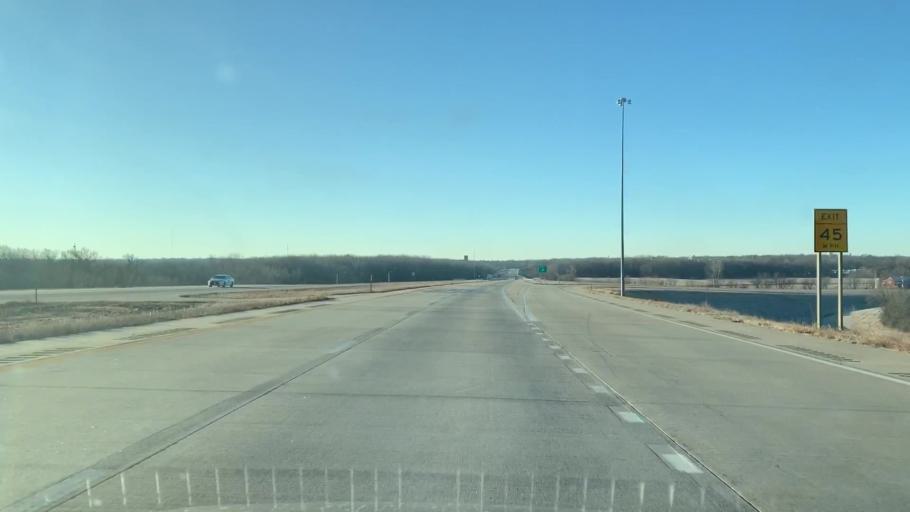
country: US
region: Kansas
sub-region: Bourbon County
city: Fort Scott
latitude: 37.8591
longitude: -94.7027
